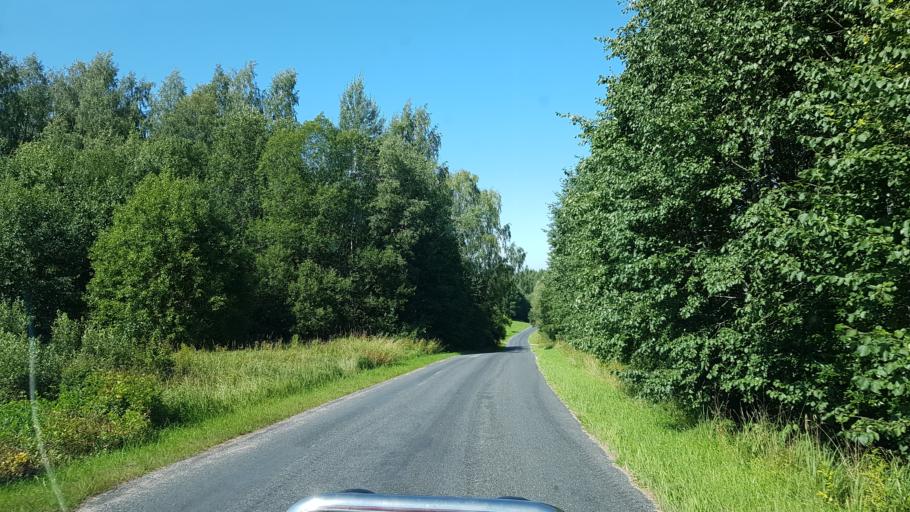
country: EE
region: Vorumaa
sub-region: Voru linn
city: Voru
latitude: 57.7903
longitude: 27.2381
